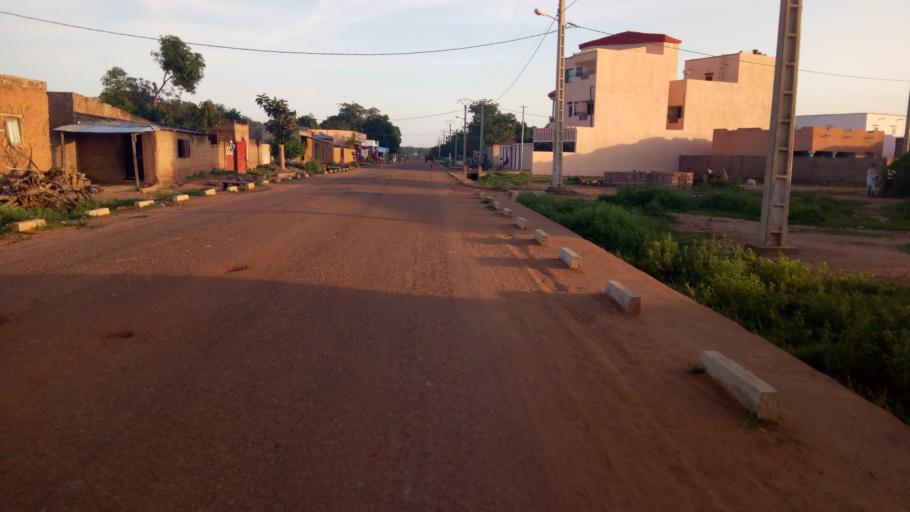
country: ML
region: Sikasso
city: Koutiala
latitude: 12.4077
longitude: -5.4450
